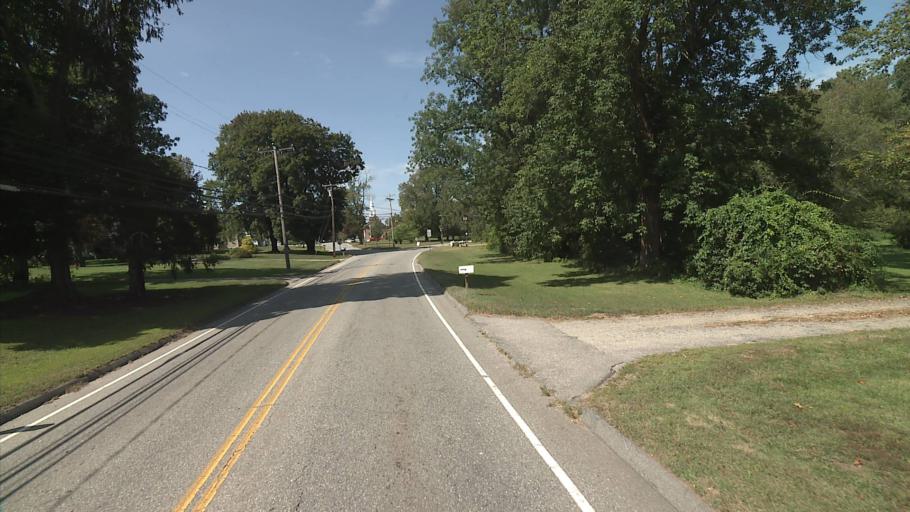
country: US
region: Connecticut
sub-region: Windham County
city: South Windham
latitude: 41.6339
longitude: -72.2106
